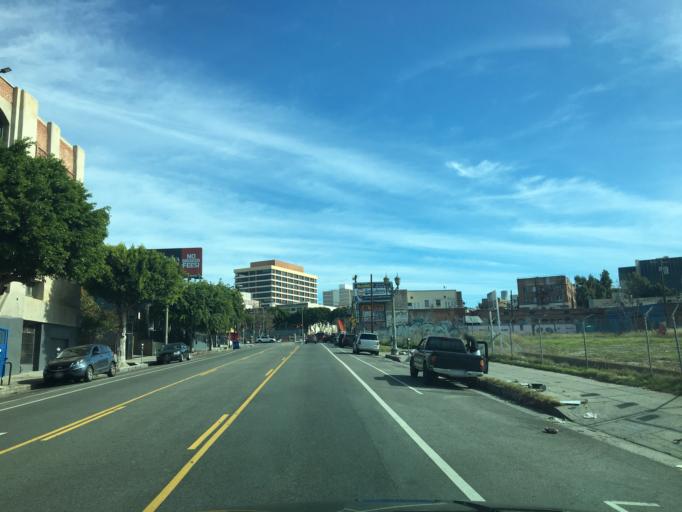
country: US
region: California
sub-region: Los Angeles County
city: Echo Park
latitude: 34.0598
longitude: -118.2857
